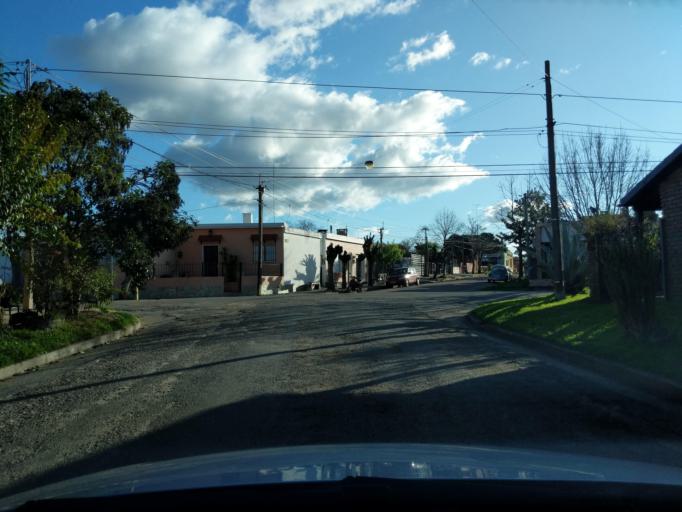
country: UY
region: Florida
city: Florida
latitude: -34.1010
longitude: -56.2249
